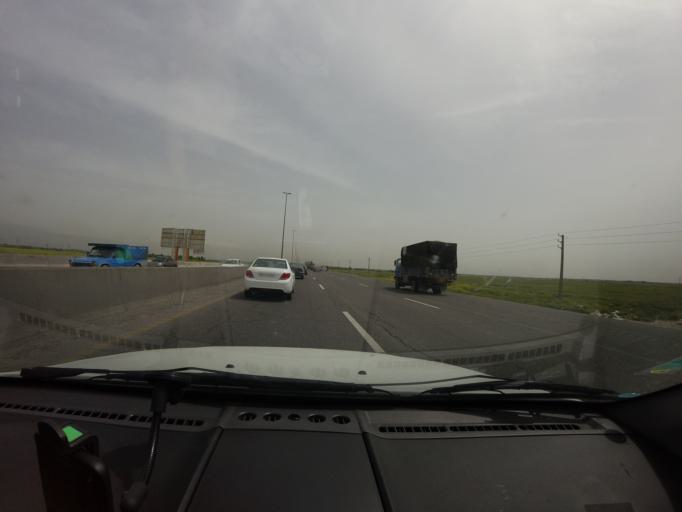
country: IR
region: Tehran
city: Eslamshahr
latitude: 35.5874
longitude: 51.1687
